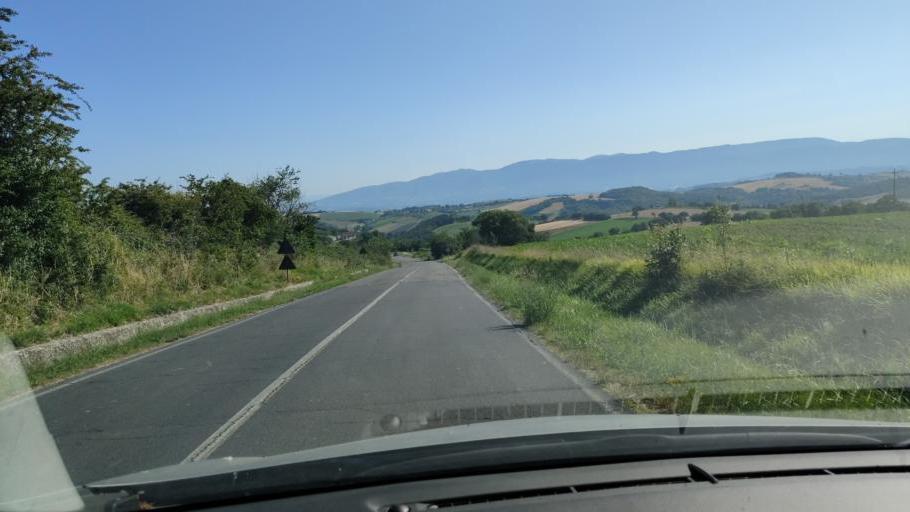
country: IT
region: Umbria
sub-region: Provincia di Terni
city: Avigliano Umbro
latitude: 42.6758
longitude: 12.4408
